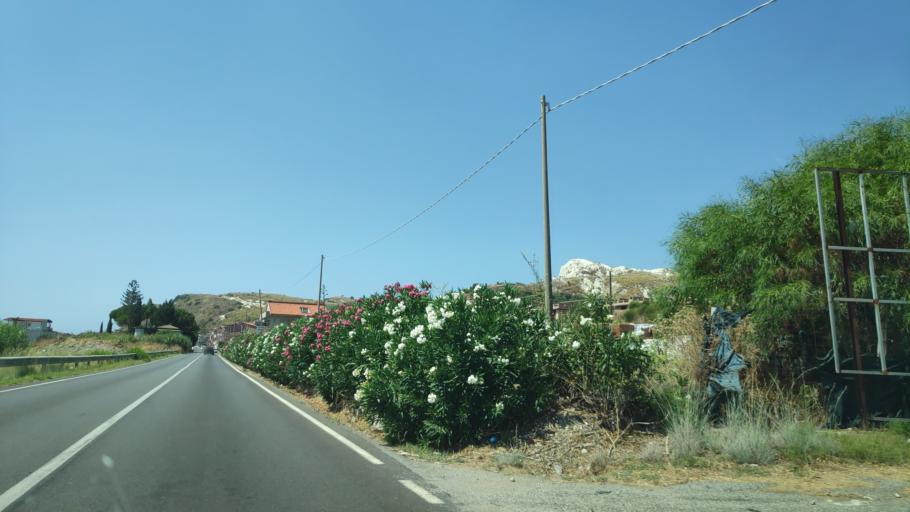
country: IT
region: Calabria
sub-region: Provincia di Reggio Calabria
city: Weather Station
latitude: 37.9338
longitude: 16.0707
